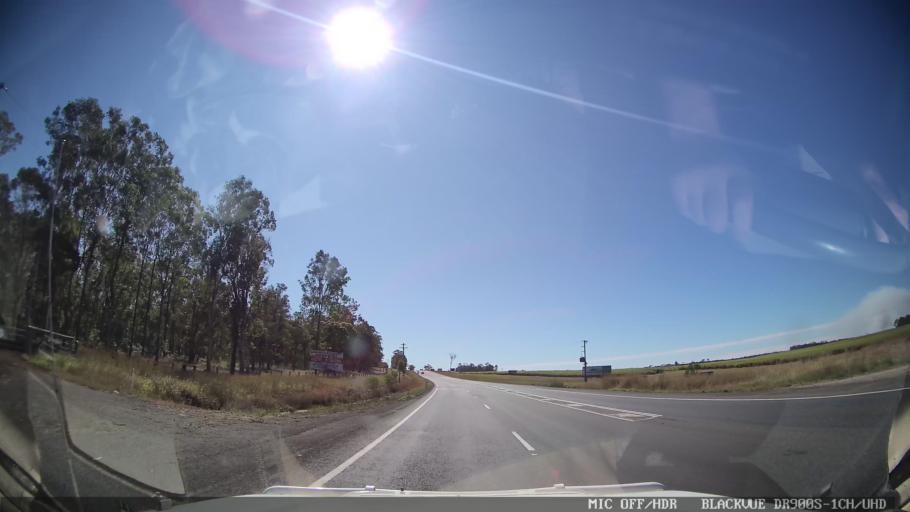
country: AU
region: Queensland
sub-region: Fraser Coast
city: Maryborough
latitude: -25.6448
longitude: 152.6376
